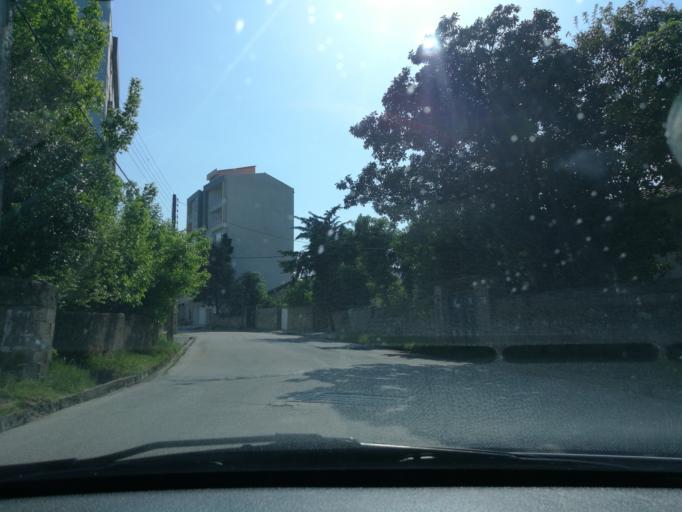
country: IR
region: Mazandaran
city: Chalus
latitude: 36.6616
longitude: 51.4288
